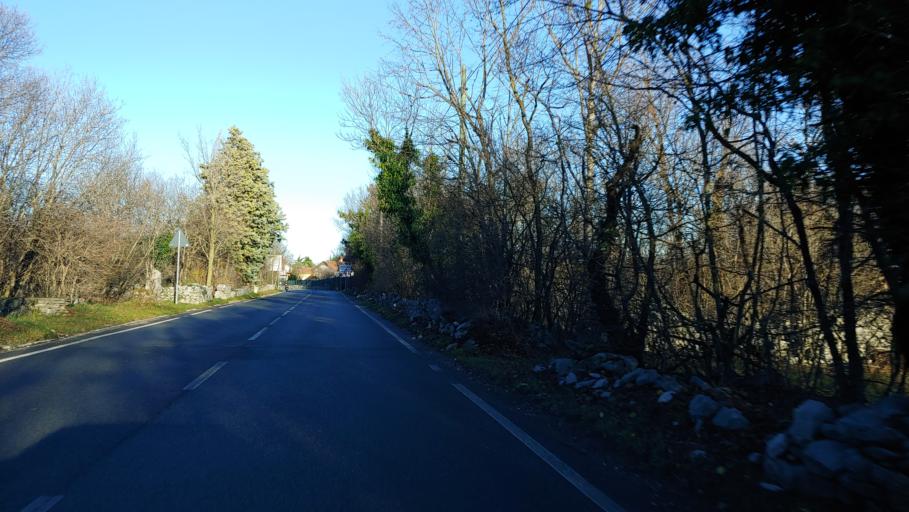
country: IT
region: Friuli Venezia Giulia
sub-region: Provincia di Trieste
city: Villa Opicina
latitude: 45.6683
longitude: 13.8296
